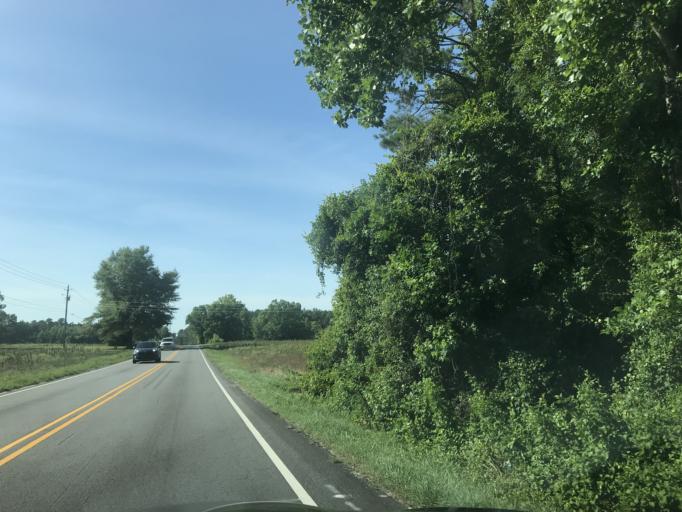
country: US
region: North Carolina
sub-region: Johnston County
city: Clayton
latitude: 35.6545
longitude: -78.5418
